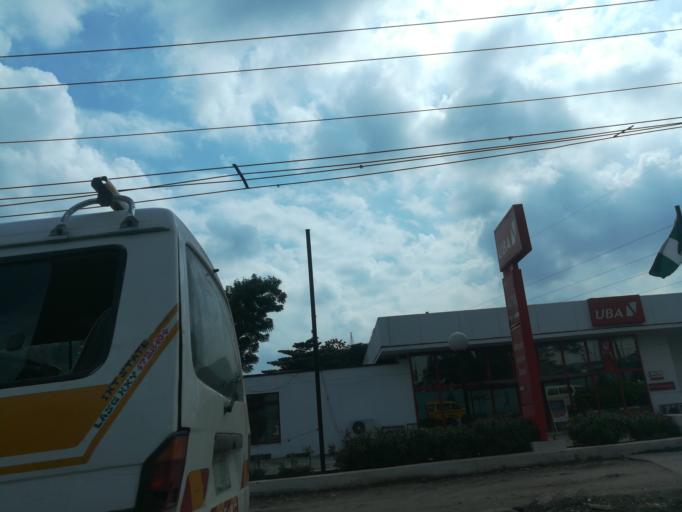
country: NG
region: Lagos
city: Somolu
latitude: 6.5493
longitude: 3.3565
